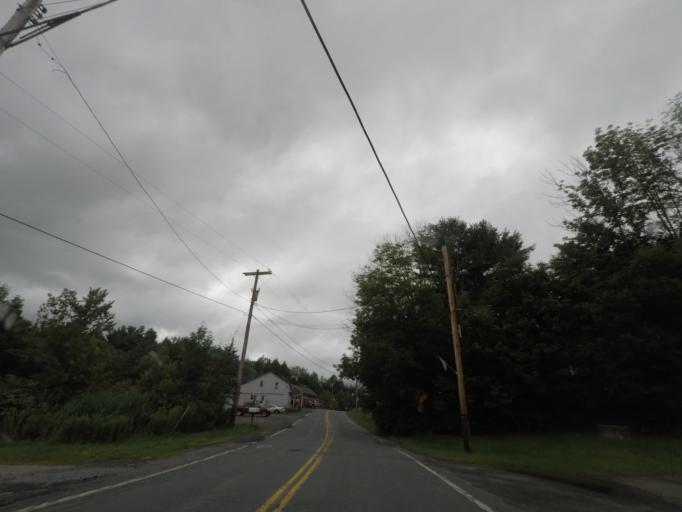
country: US
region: New York
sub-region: Rensselaer County
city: Poestenkill
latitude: 42.6826
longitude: -73.4969
